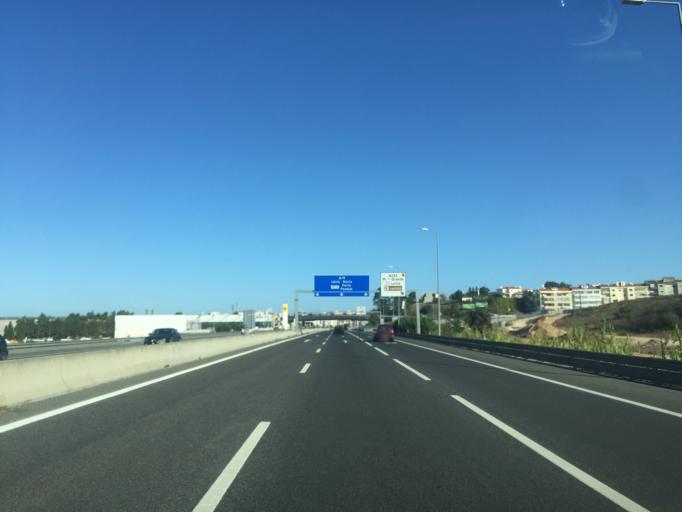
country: PT
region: Leiria
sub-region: Leiria
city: Leiria
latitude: 39.7422
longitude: -8.8192
